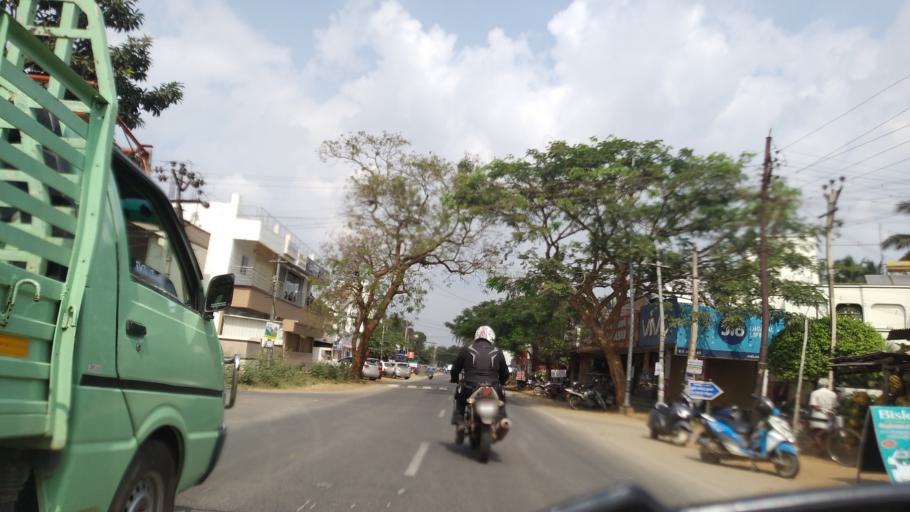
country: IN
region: Tamil Nadu
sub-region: Coimbatore
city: Perur
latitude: 10.9488
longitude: 76.9352
